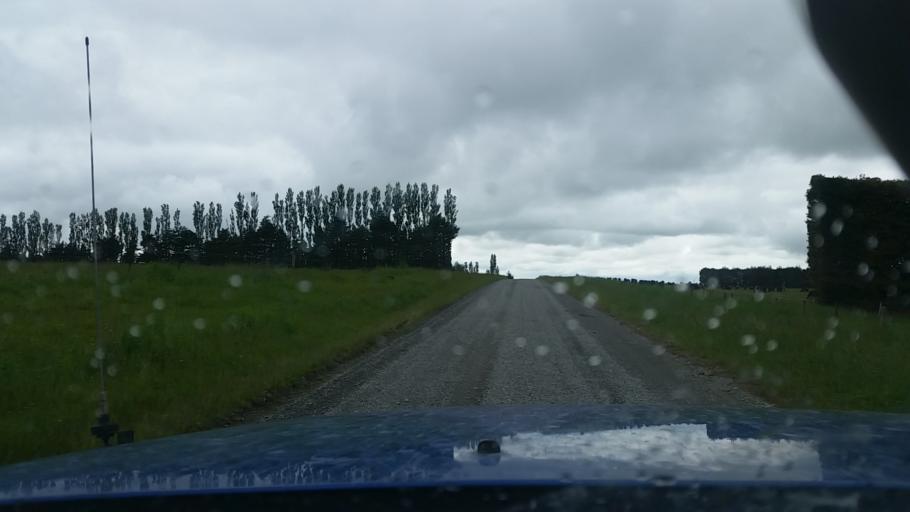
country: NZ
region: Canterbury
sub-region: Ashburton District
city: Methven
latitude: -43.6928
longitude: 171.4003
